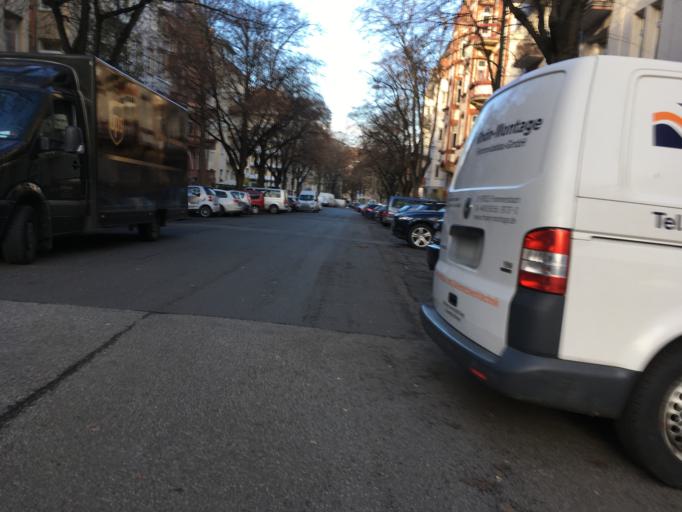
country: DE
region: Hesse
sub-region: Regierungsbezirk Darmstadt
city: Wiesbaden
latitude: 50.0708
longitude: 8.2331
